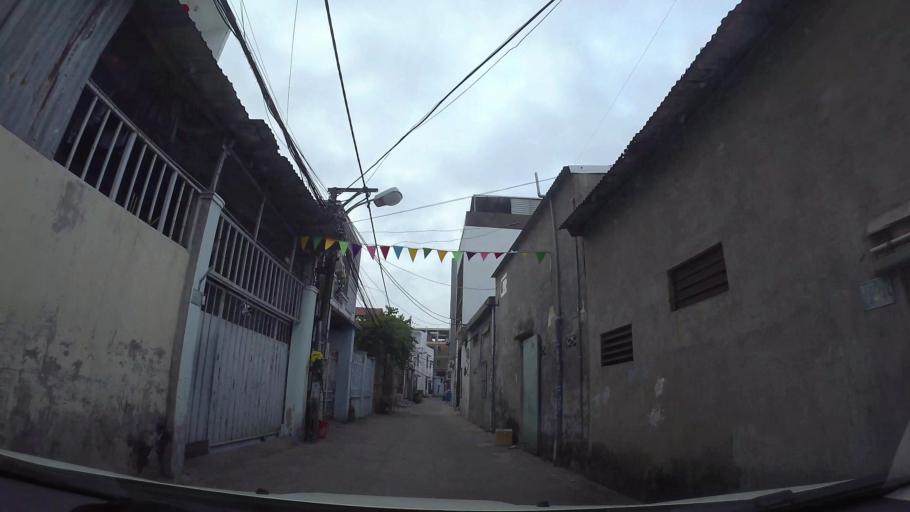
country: VN
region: Da Nang
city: Son Tra
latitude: 16.0587
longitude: 108.2388
